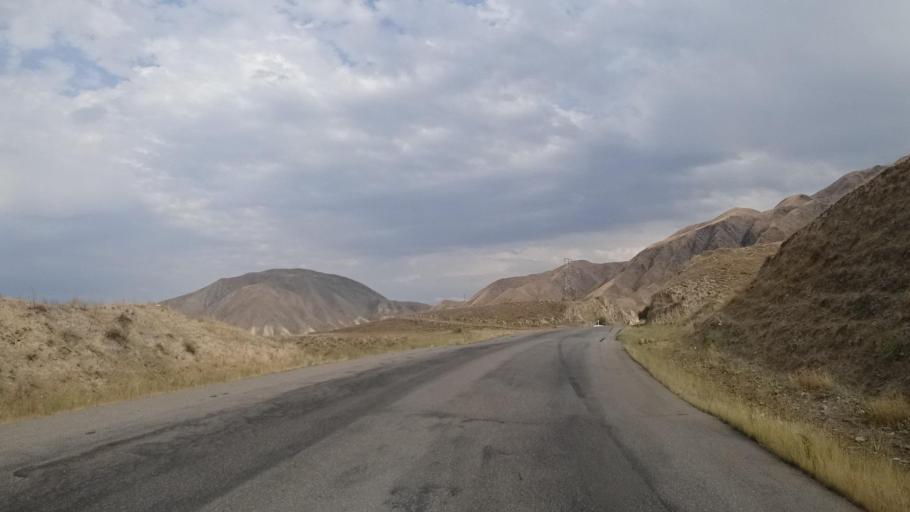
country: KG
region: Jalal-Abad
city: Toktogul
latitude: 41.7824
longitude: 73.0029
